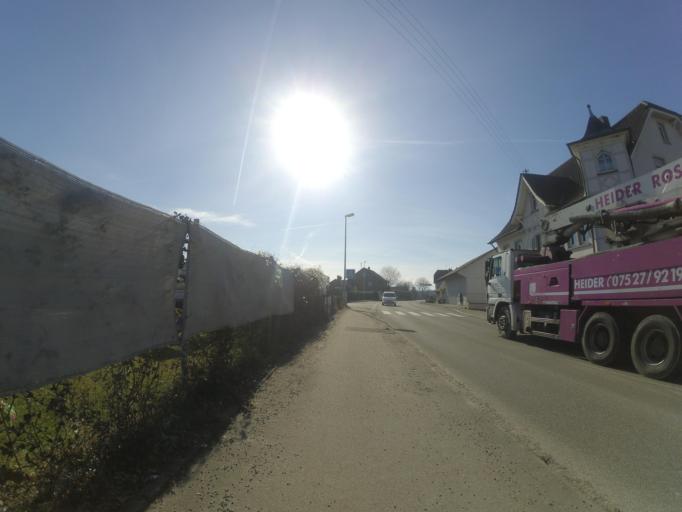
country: DE
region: Baden-Wuerttemberg
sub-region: Tuebingen Region
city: Baindt
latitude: 47.8711
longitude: 9.6381
